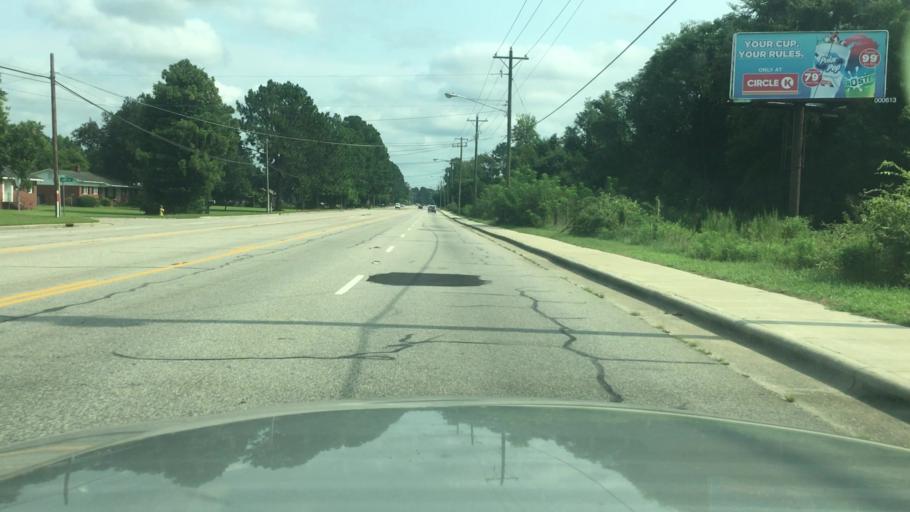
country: US
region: North Carolina
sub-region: Cumberland County
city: Fayetteville
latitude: 35.0236
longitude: -78.8418
